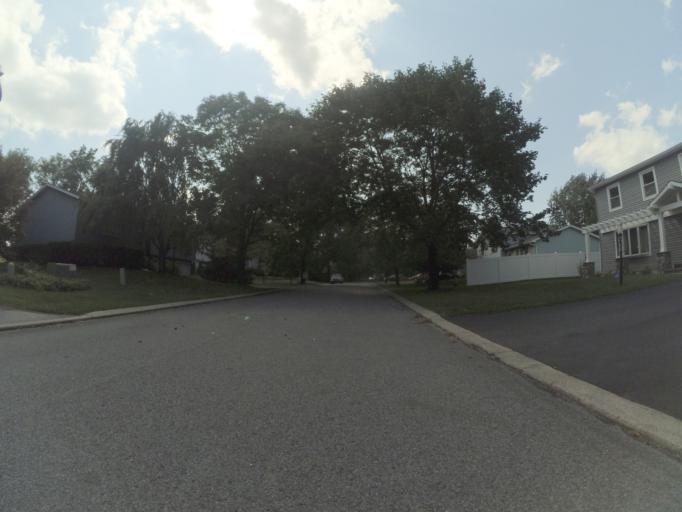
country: US
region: Pennsylvania
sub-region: Centre County
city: Houserville
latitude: 40.8280
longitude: -77.8245
